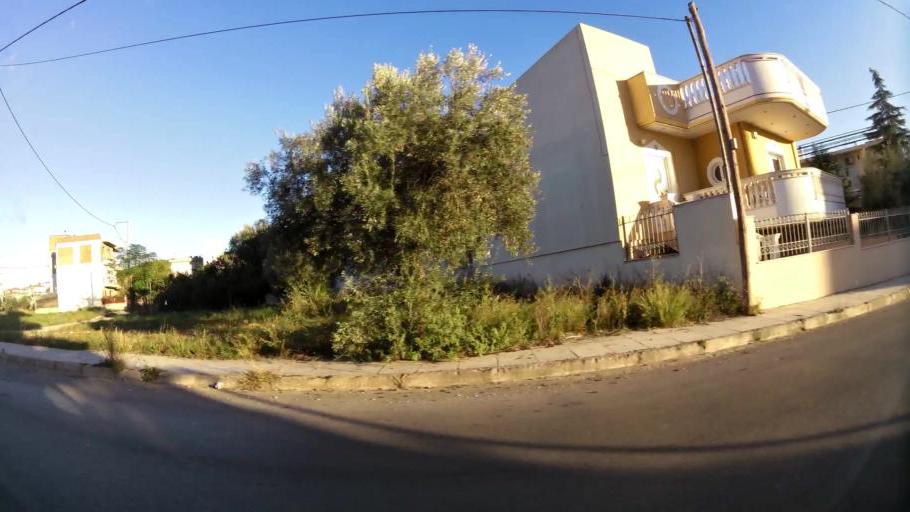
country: GR
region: Attica
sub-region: Nomarchia Dytikis Attikis
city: Ano Liosia
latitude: 38.0888
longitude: 23.7156
